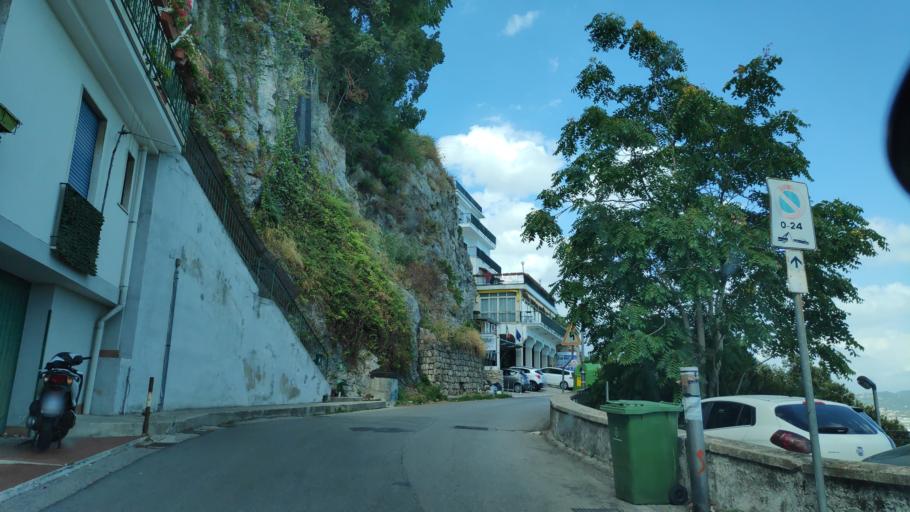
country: IT
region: Campania
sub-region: Provincia di Salerno
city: Vietri sul Mare
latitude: 40.6689
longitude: 14.7298
